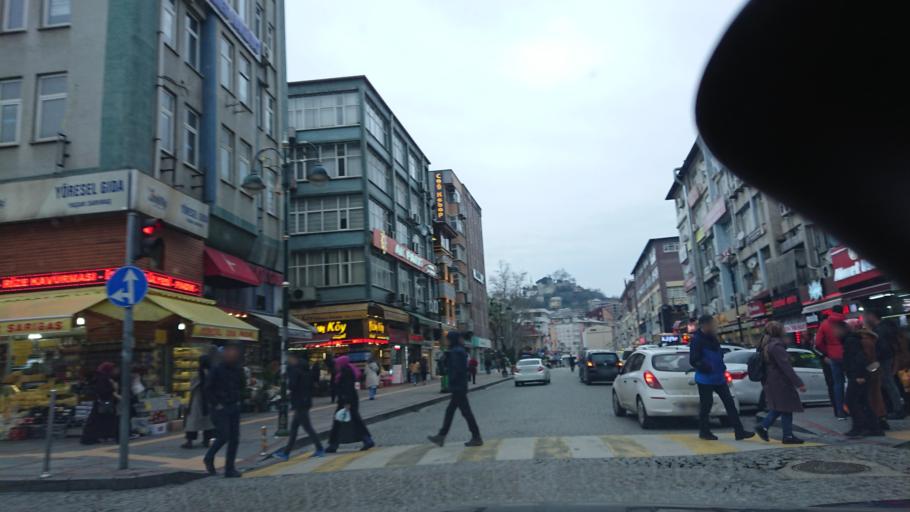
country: TR
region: Rize
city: Rize
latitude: 41.0249
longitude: 40.5199
